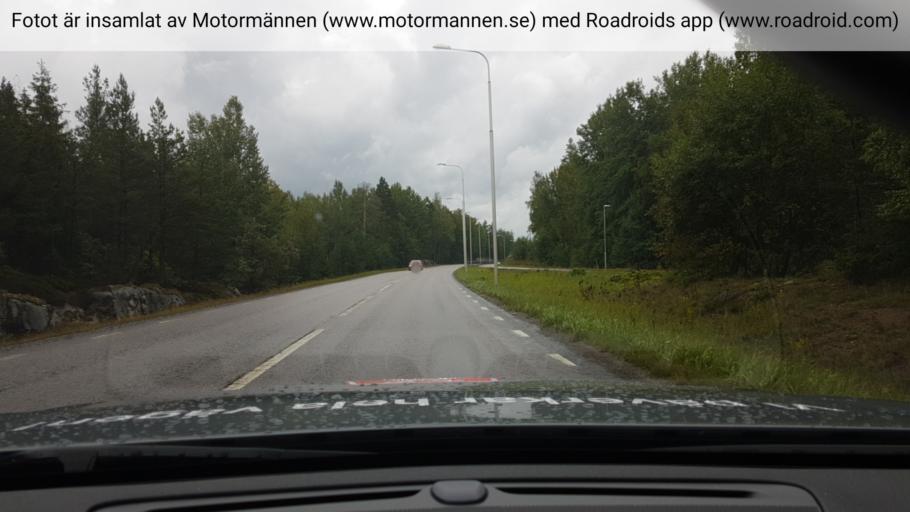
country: SE
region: Stockholm
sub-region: Botkyrka Kommun
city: Tullinge
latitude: 59.1986
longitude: 17.9288
